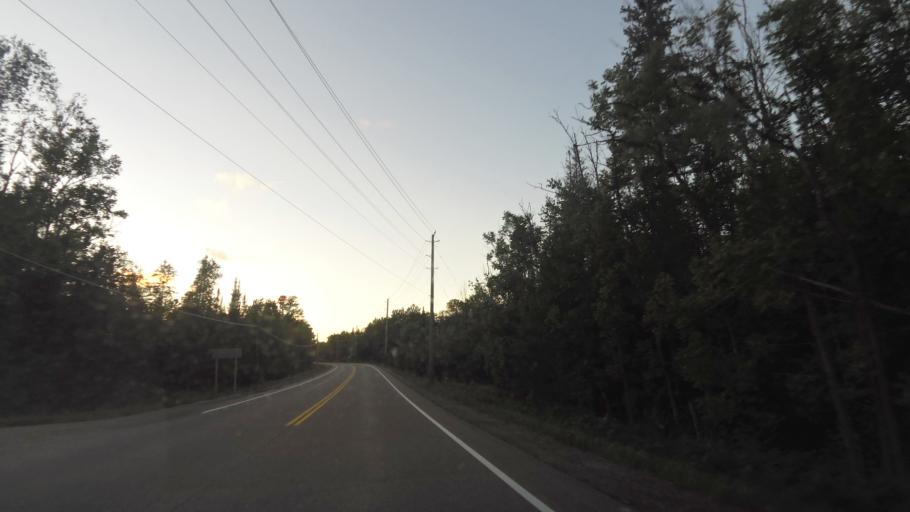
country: CA
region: Ontario
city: Bancroft
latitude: 45.0325
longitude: -78.4105
